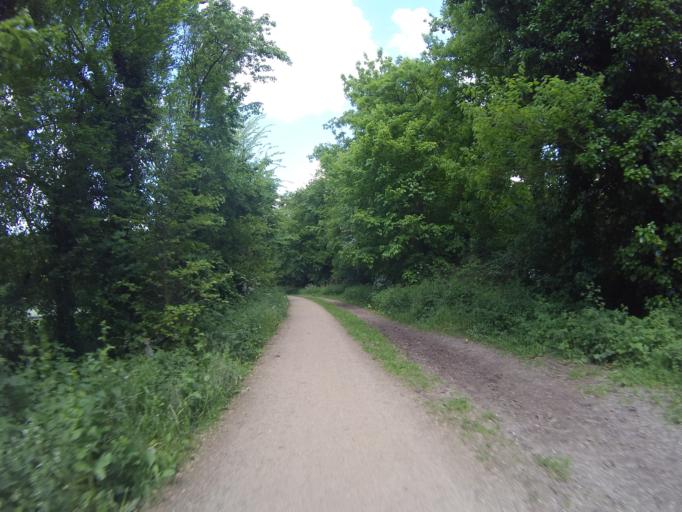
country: NL
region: North Holland
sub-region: Gemeente Laren
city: Laren
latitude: 52.2583
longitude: 5.2395
